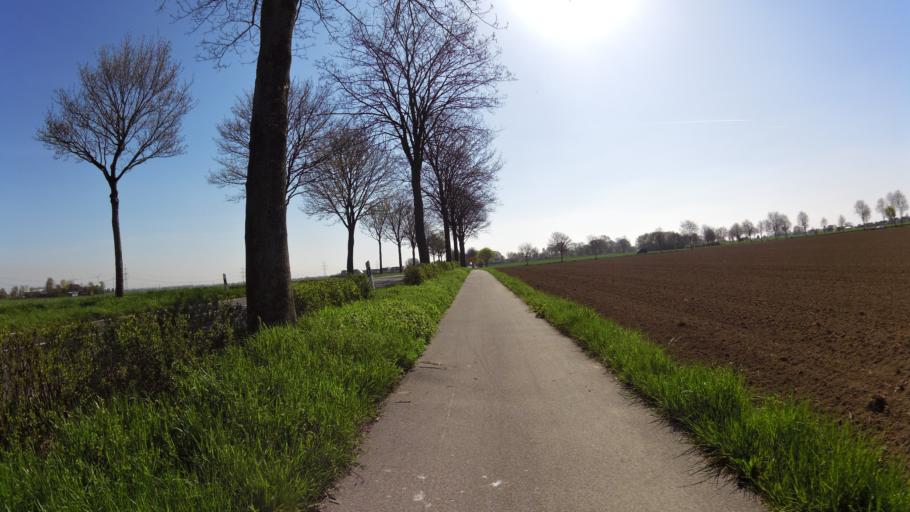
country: DE
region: North Rhine-Westphalia
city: Geilenkirchen
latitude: 50.9555
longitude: 6.1559
